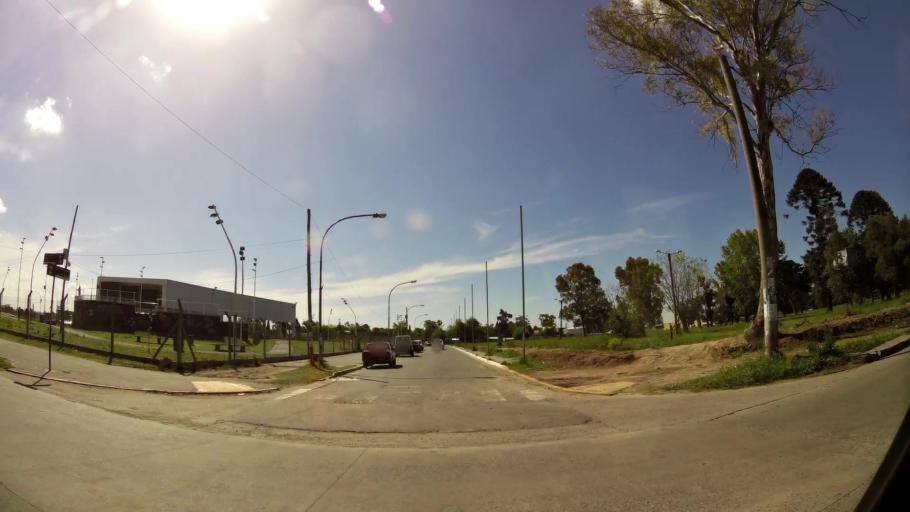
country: AR
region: Buenos Aires
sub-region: Partido de Quilmes
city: Quilmes
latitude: -34.7936
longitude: -58.2517
